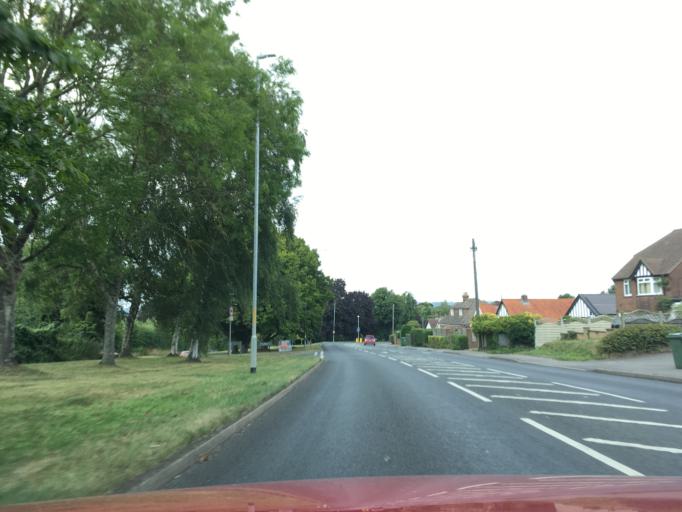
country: GB
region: England
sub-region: Kent
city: Maidstone
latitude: 51.2360
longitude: 0.5165
